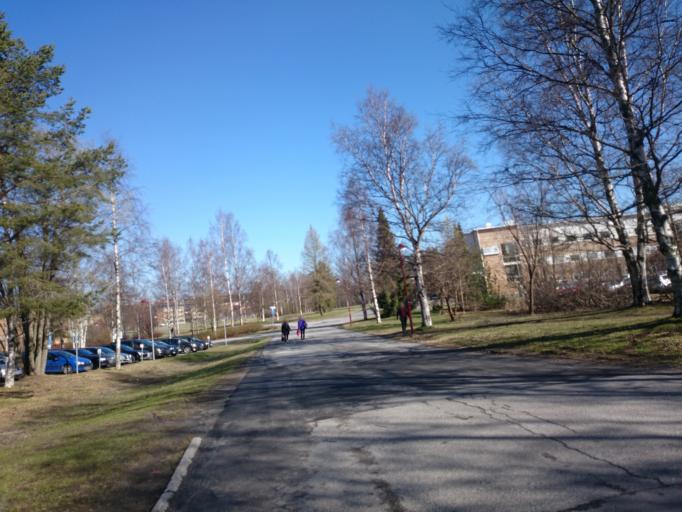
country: SE
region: Vaesterbotten
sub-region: Umea Kommun
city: Umea
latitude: 63.8195
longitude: 20.3125
